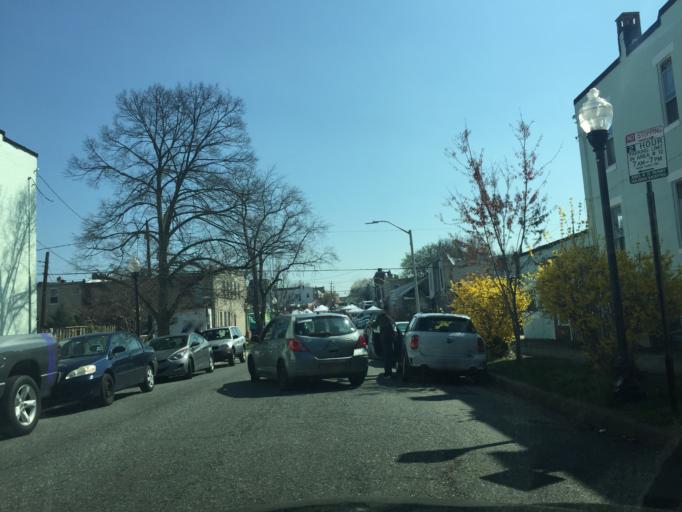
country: US
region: Maryland
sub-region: City of Baltimore
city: Baltimore
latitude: 39.3271
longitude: -76.6120
